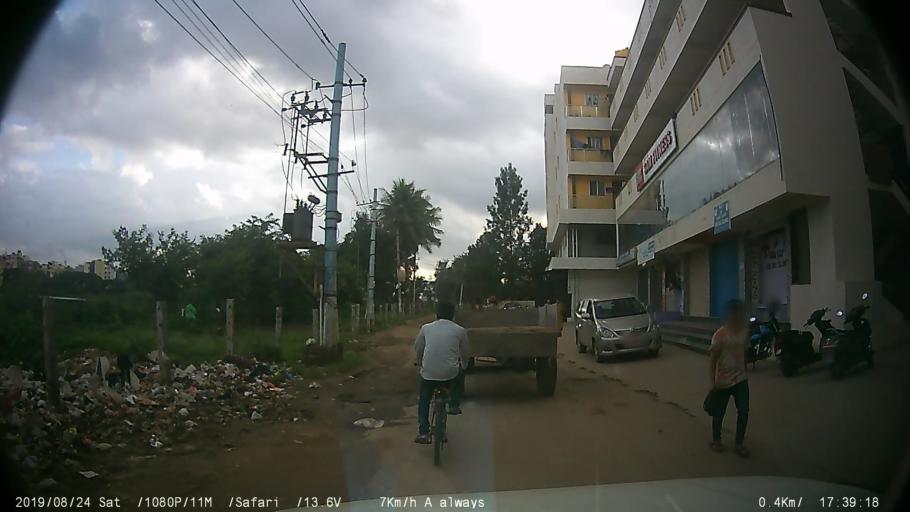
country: IN
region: Karnataka
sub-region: Bangalore Urban
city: Anekal
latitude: 12.8279
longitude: 77.6879
